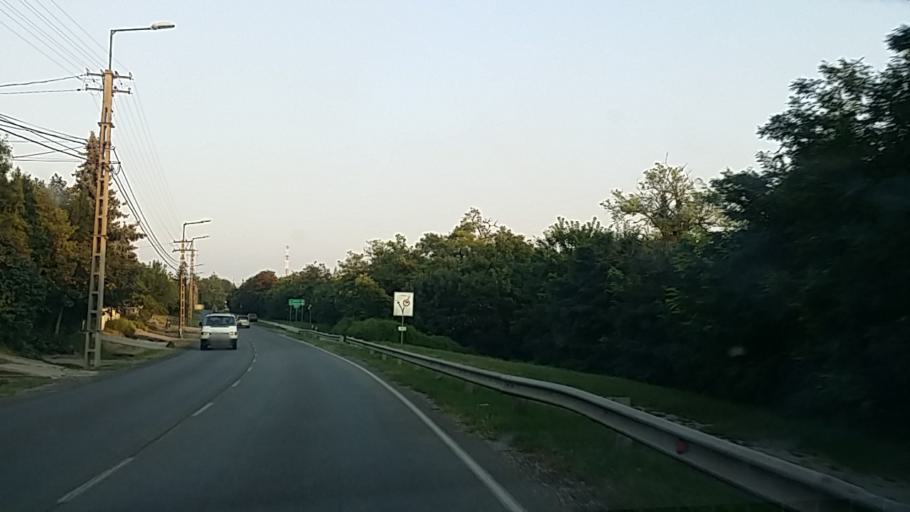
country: HU
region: Fejer
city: dunaujvaros
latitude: 46.9851
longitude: 18.9337
